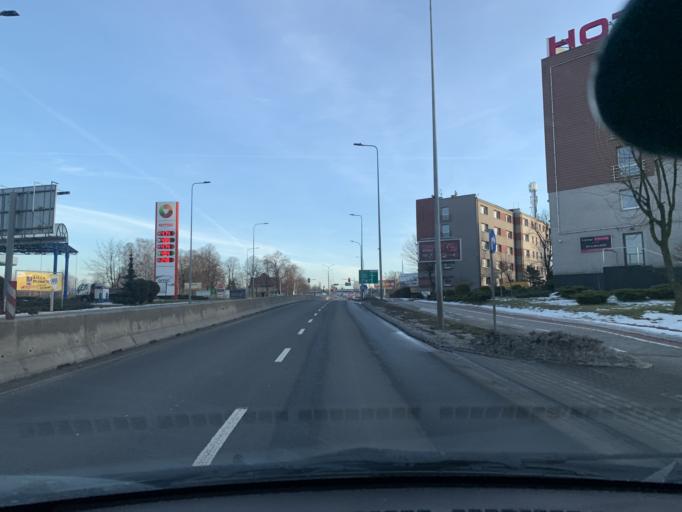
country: PL
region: Silesian Voivodeship
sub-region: Powiat tarnogorski
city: Radzionkow
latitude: 50.3718
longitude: 18.8939
